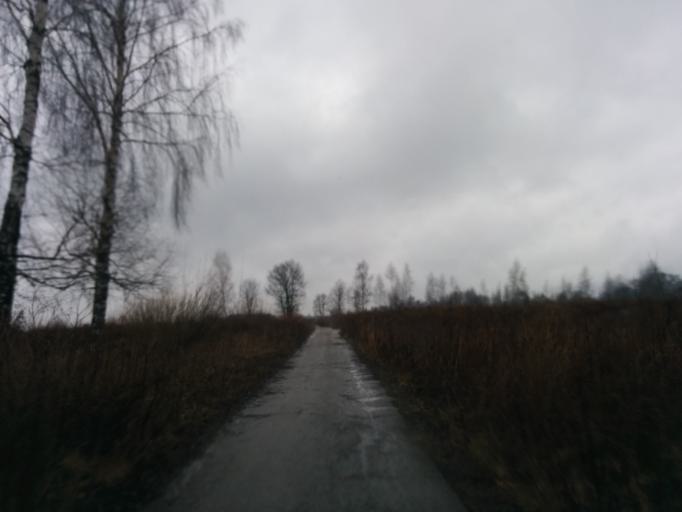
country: LV
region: Jelgava
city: Jelgava
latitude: 56.6696
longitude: 23.7127
